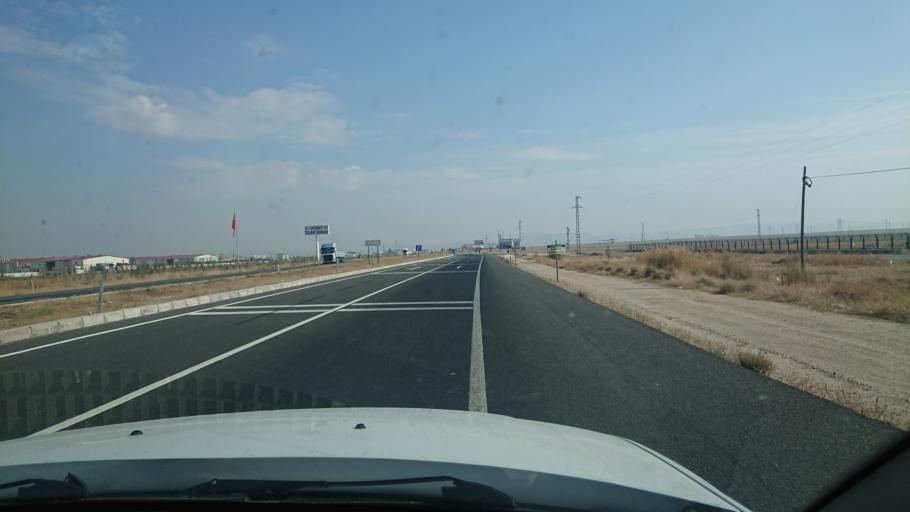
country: TR
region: Aksaray
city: Aksaray
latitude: 38.3354
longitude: 33.9301
